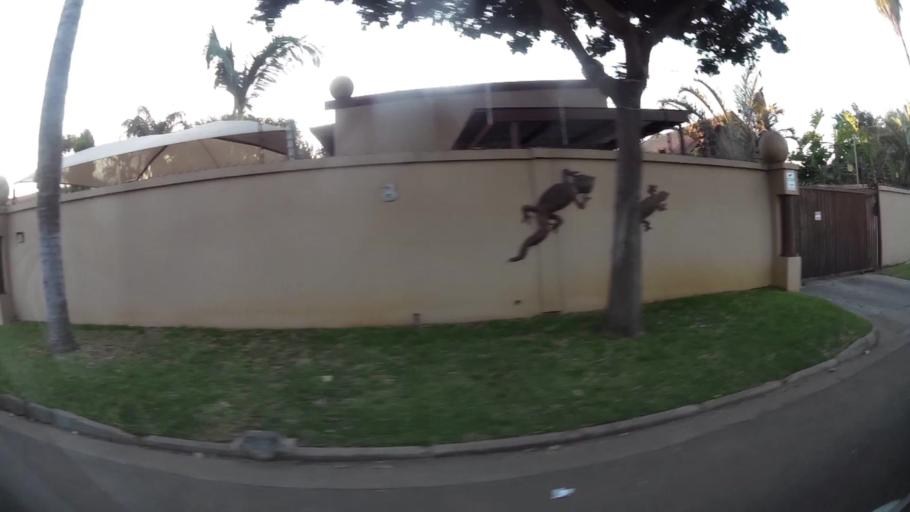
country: ZA
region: North-West
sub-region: Bojanala Platinum District Municipality
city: Rustenburg
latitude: -25.6644
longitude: 27.2475
